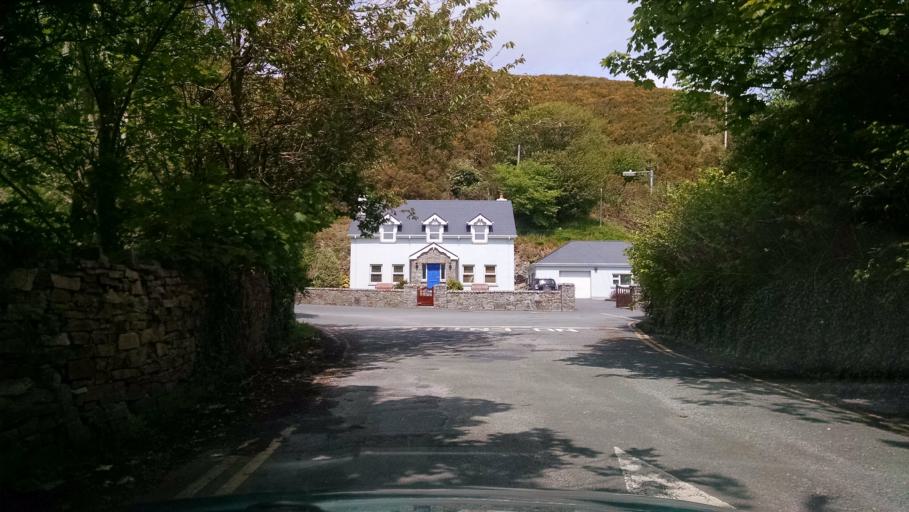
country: IE
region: Connaught
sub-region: County Galway
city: Clifden
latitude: 53.4886
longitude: -10.0269
